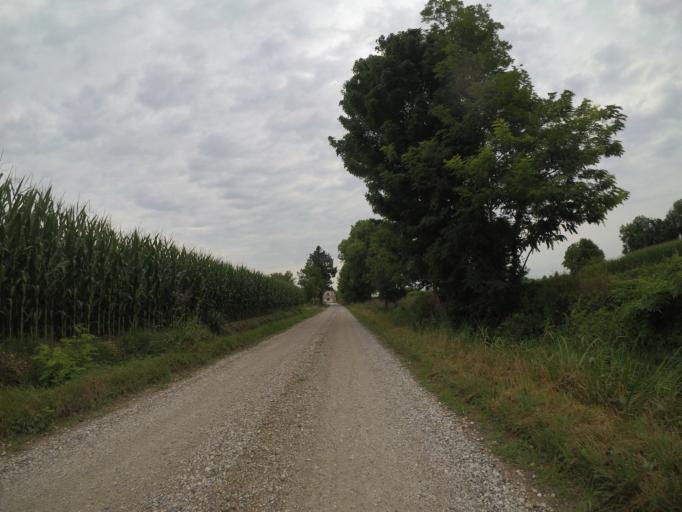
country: IT
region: Friuli Venezia Giulia
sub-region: Provincia di Udine
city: Varmo
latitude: 45.8768
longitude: 13.0101
